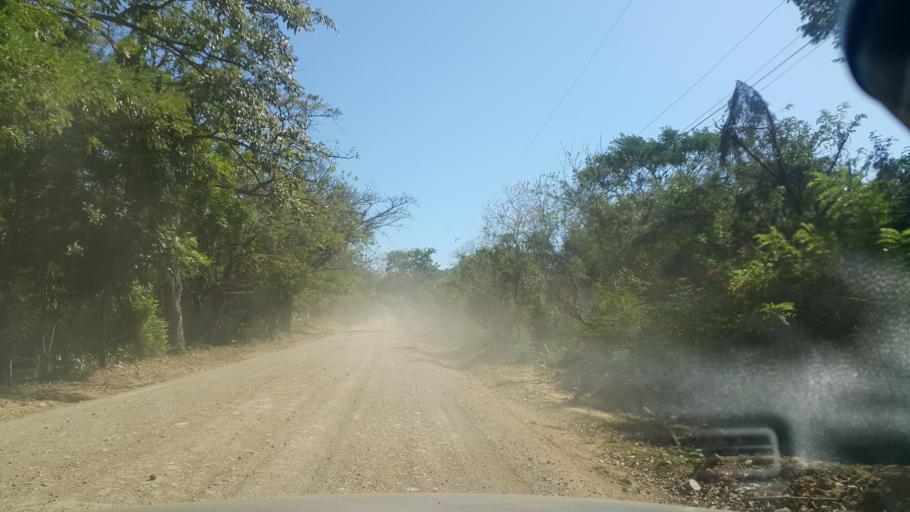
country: NI
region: Rivas
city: San Juan del Sur
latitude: 11.2839
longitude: -85.8894
